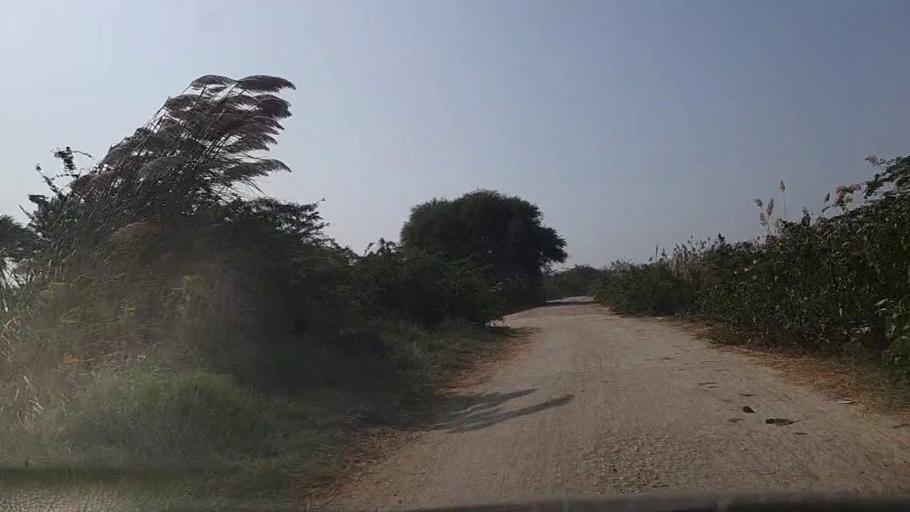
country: PK
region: Sindh
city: Gharo
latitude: 24.7052
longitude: 67.6472
